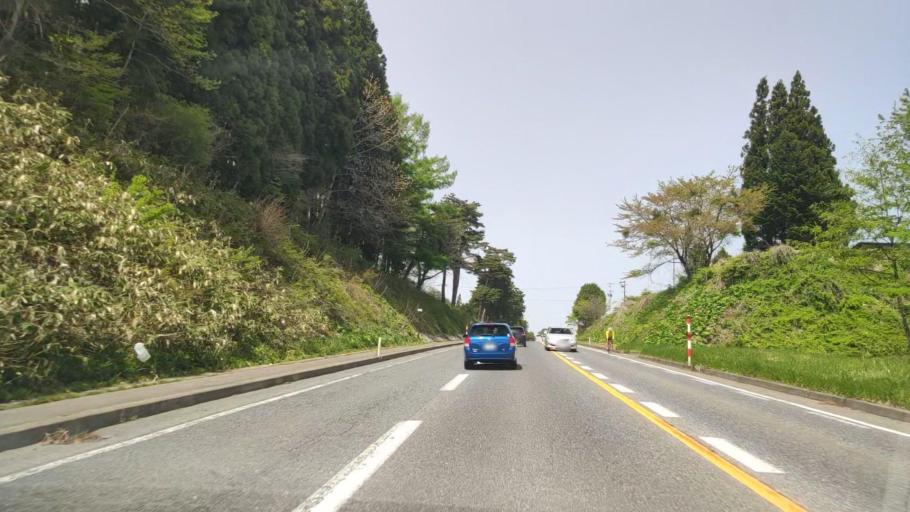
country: JP
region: Aomori
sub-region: Misawa Shi
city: Inuotose
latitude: 40.6668
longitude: 141.1856
